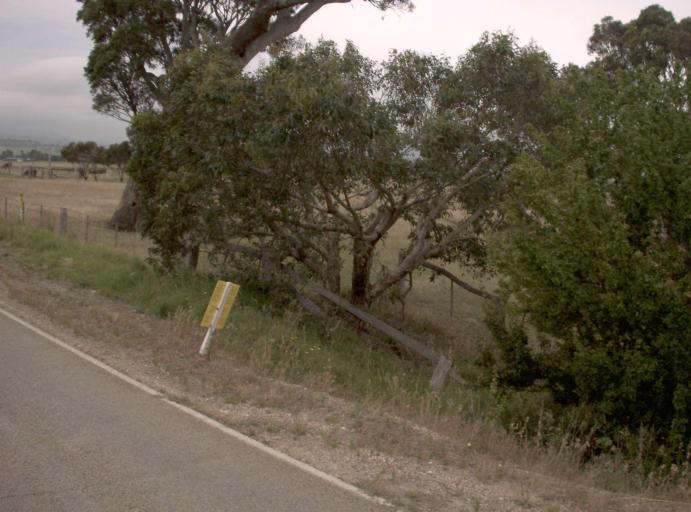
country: AU
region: Victoria
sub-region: East Gippsland
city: Bairnsdale
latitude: -37.8138
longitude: 147.4369
